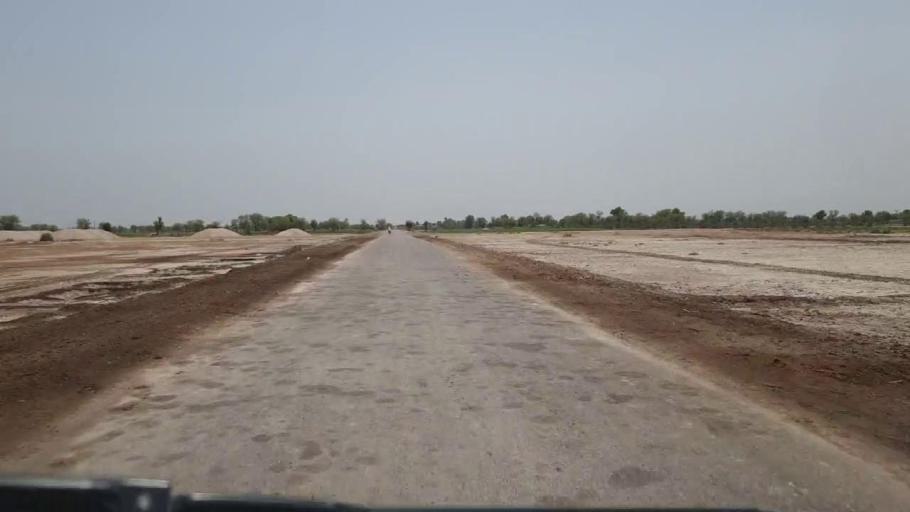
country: PK
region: Sindh
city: Daulatpur
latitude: 26.4505
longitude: 68.1171
